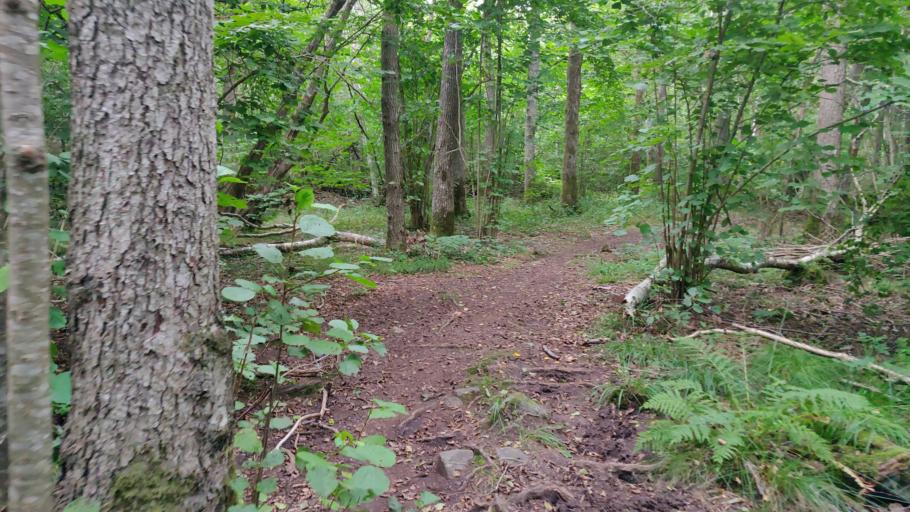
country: SE
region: Vaestra Goetaland
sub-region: Goteborg
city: Torslanda
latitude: 57.7836
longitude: 11.8204
